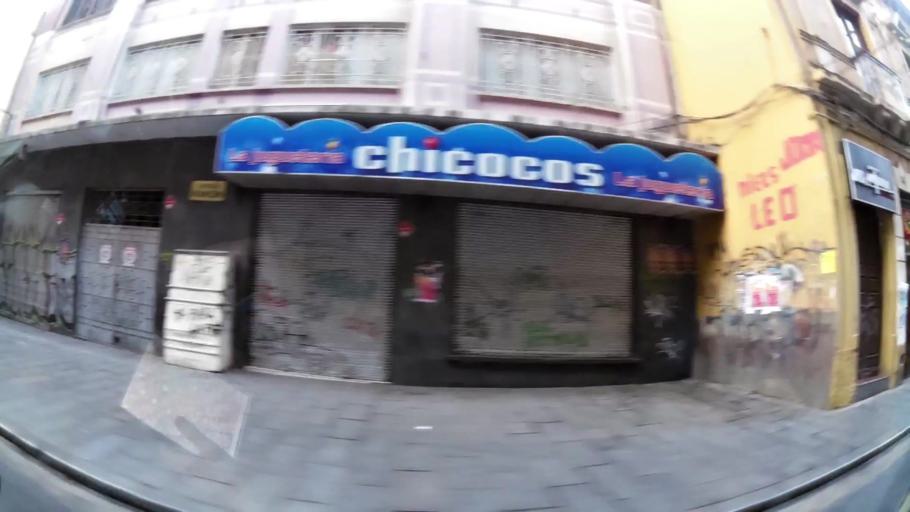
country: BO
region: La Paz
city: La Paz
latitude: -16.4967
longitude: -68.1344
